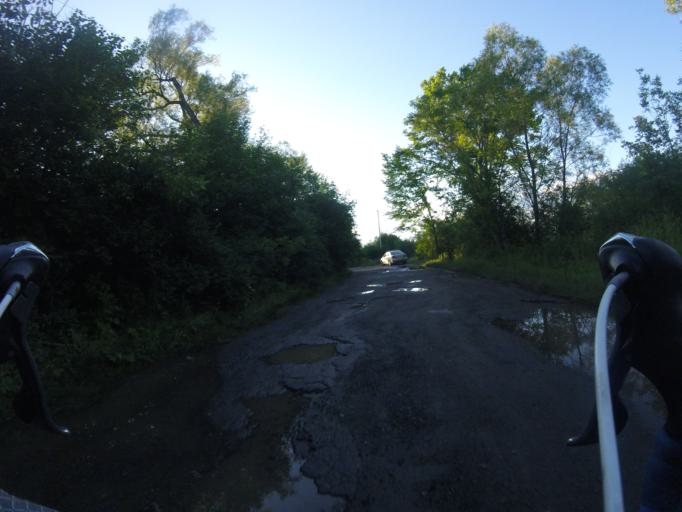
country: CA
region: Ontario
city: Bells Corners
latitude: 45.3655
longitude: -75.8804
